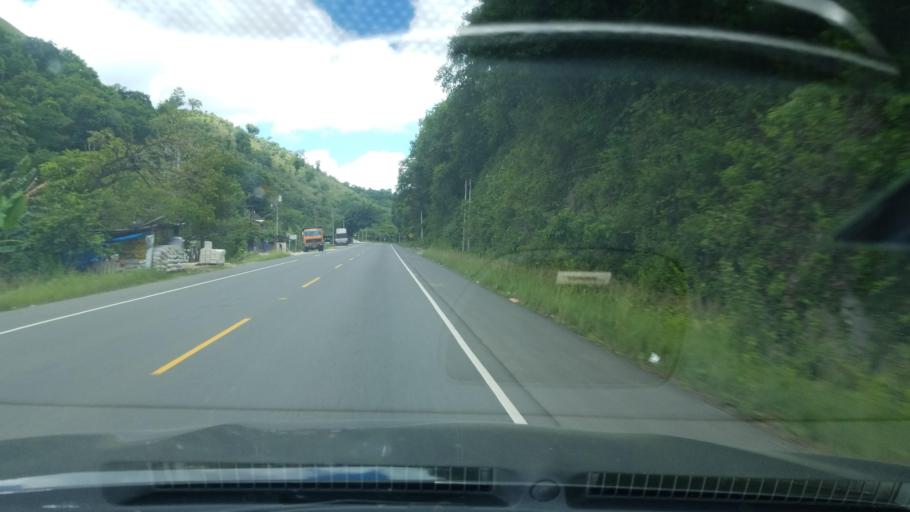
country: HN
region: Francisco Morazan
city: Talanga
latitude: 14.3742
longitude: -87.1369
